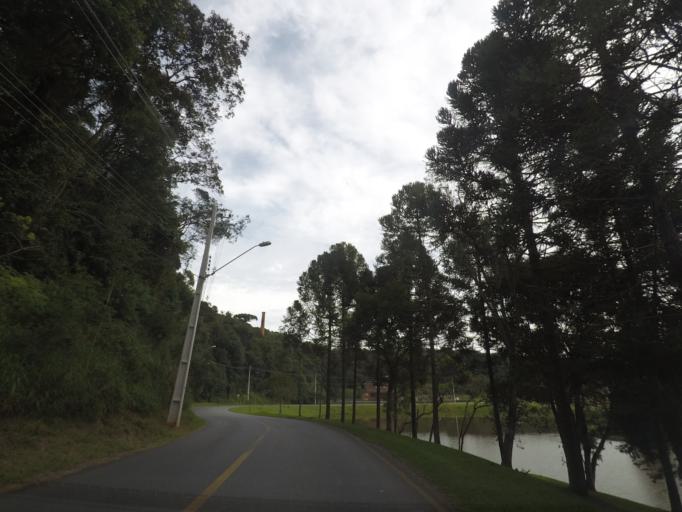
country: BR
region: Parana
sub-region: Curitiba
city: Curitiba
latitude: -25.3941
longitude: -49.3060
